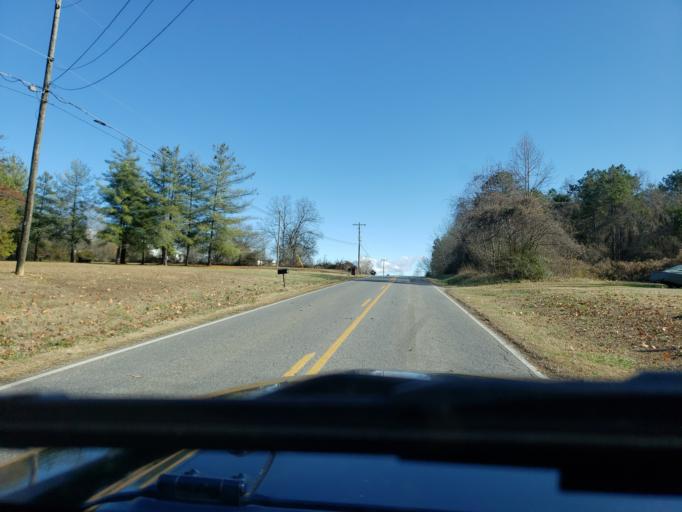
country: US
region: South Carolina
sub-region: Cherokee County
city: Blacksburg
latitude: 35.1906
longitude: -81.4719
